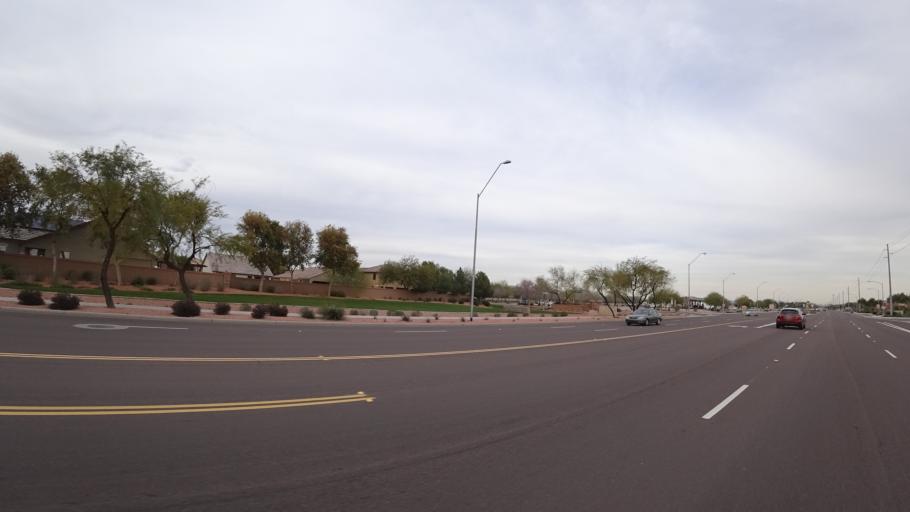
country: US
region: Arizona
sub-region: Maricopa County
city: Surprise
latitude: 33.6092
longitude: -112.3644
